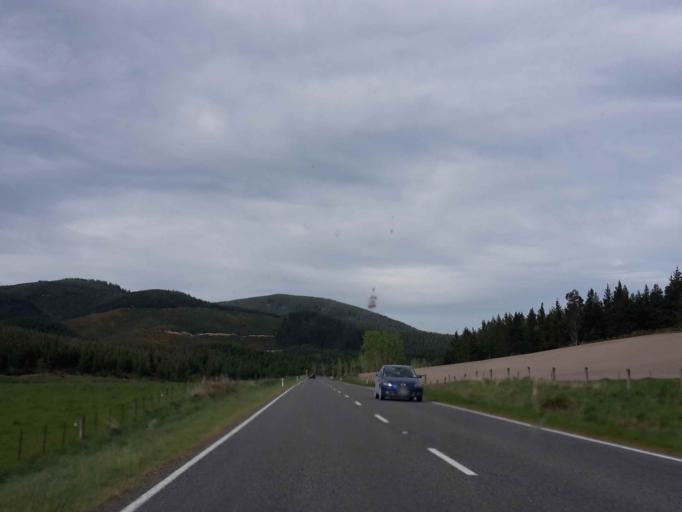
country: NZ
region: Canterbury
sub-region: Timaru District
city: Pleasant Point
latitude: -44.1211
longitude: 171.0514
